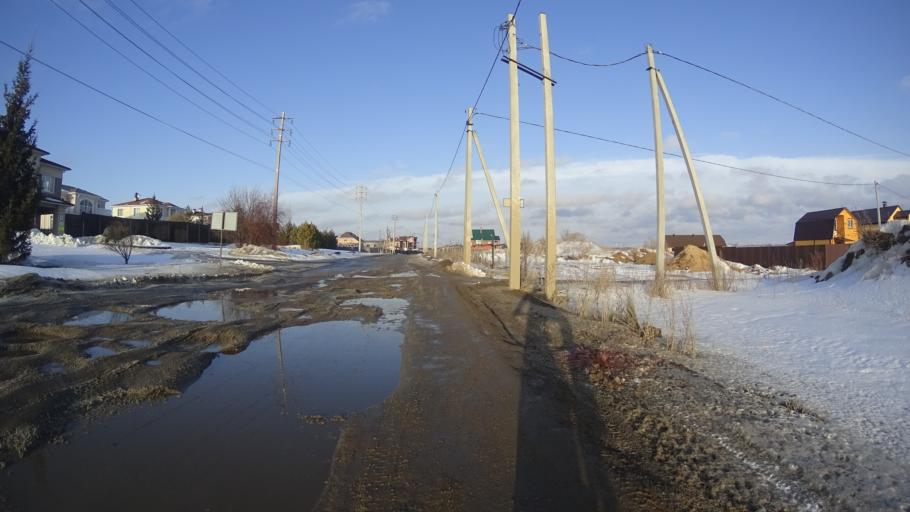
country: RU
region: Chelyabinsk
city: Sargazy
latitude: 55.1091
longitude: 61.2740
